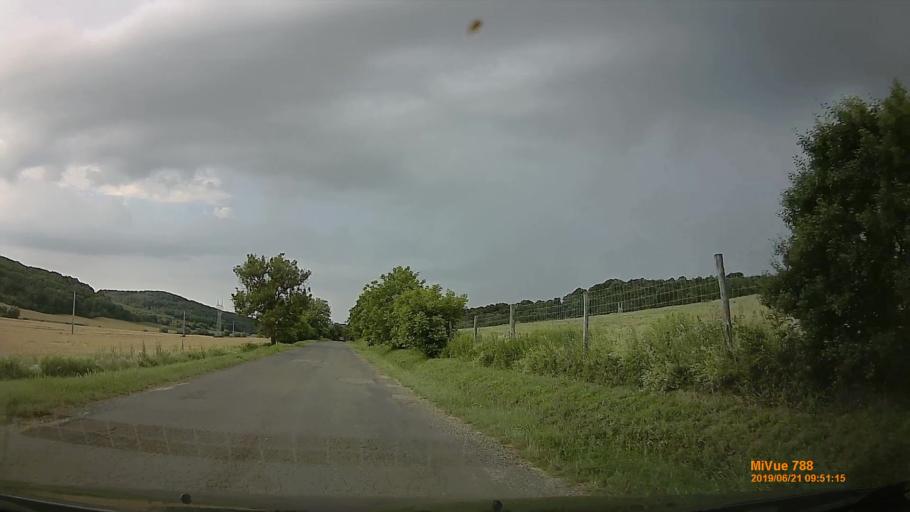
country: HU
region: Baranya
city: Sasd
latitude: 46.2539
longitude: 18.0232
